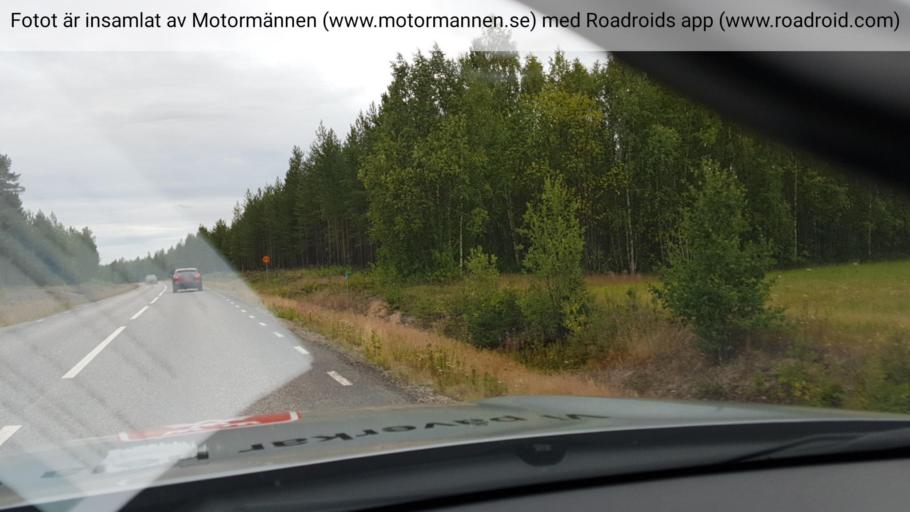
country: SE
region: Norrbotten
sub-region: Overkalix Kommun
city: OEverkalix
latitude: 66.5305
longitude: 22.7572
